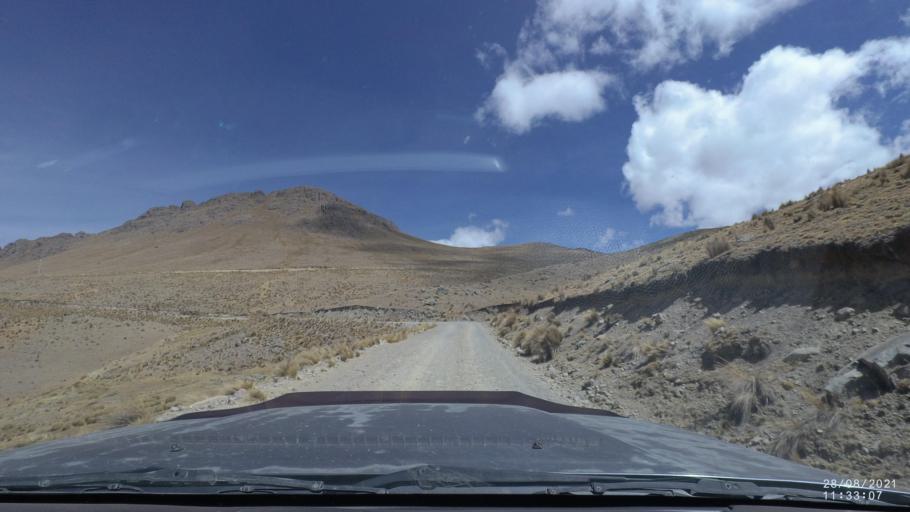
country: BO
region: Cochabamba
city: Sipe Sipe
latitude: -17.1843
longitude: -66.3702
